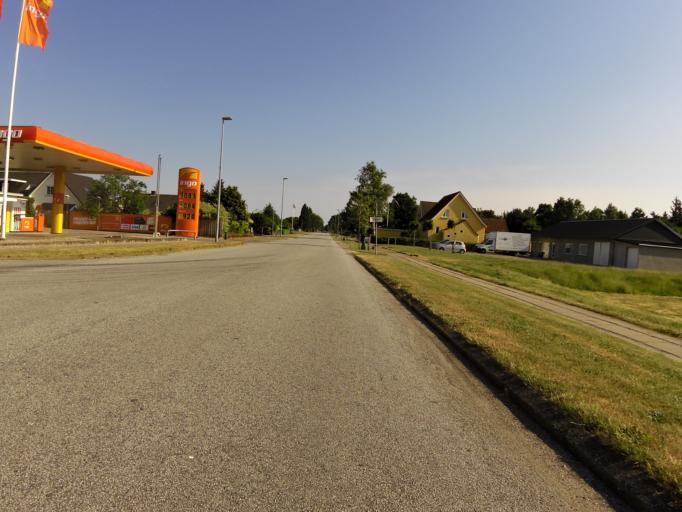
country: DK
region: South Denmark
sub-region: Haderslev Kommune
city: Vojens
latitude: 55.2439
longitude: 9.2930
